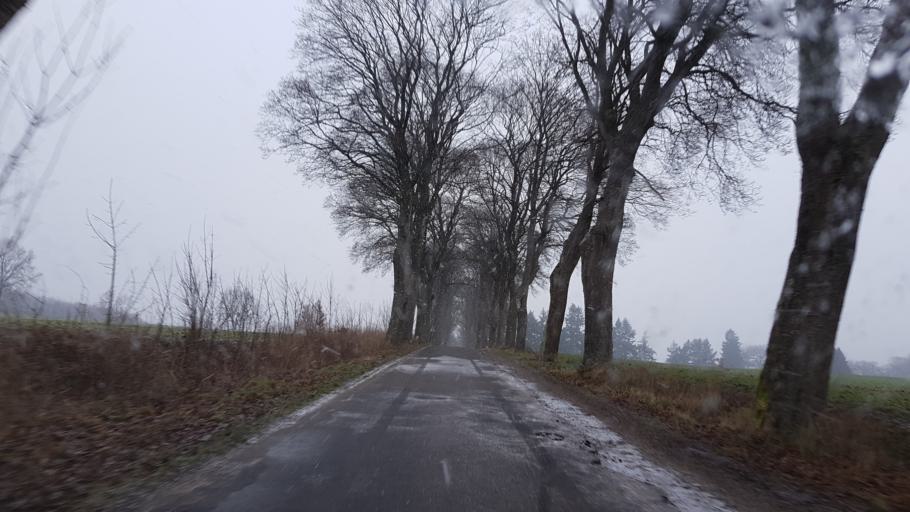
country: PL
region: West Pomeranian Voivodeship
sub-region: Powiat slawienski
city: Slawno
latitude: 54.2758
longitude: 16.5986
